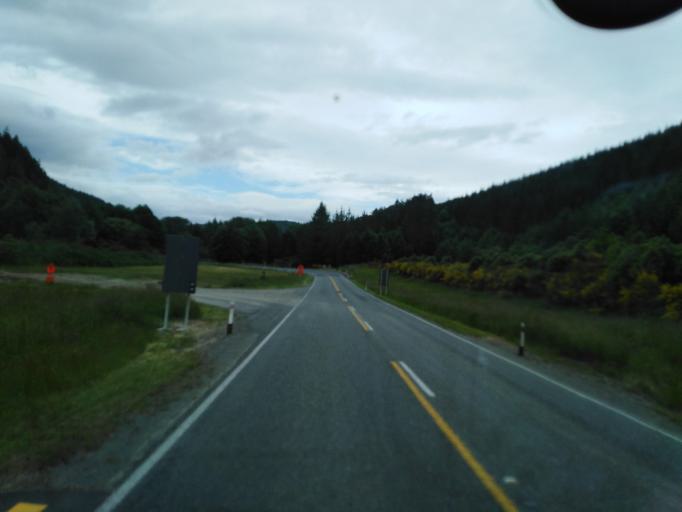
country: NZ
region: Tasman
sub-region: Tasman District
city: Wakefield
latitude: -41.4846
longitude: 172.8872
